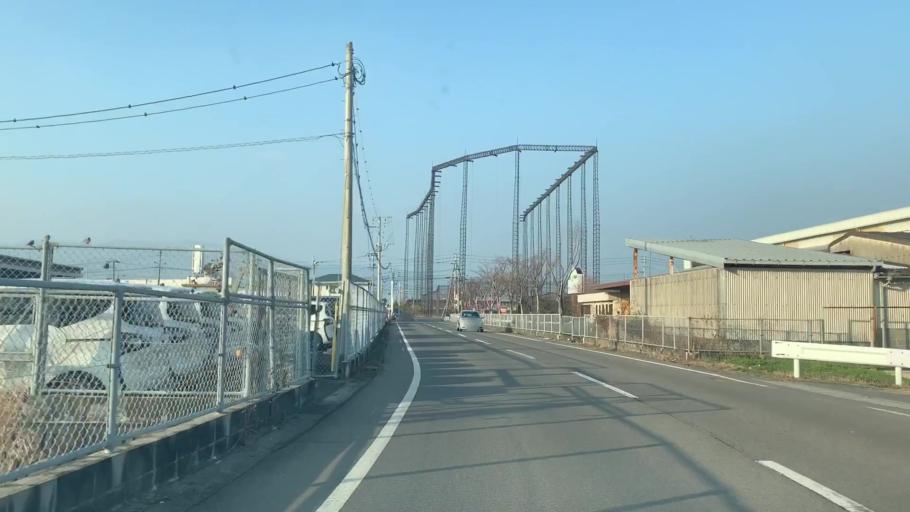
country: JP
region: Saga Prefecture
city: Saga-shi
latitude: 33.2638
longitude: 130.2479
